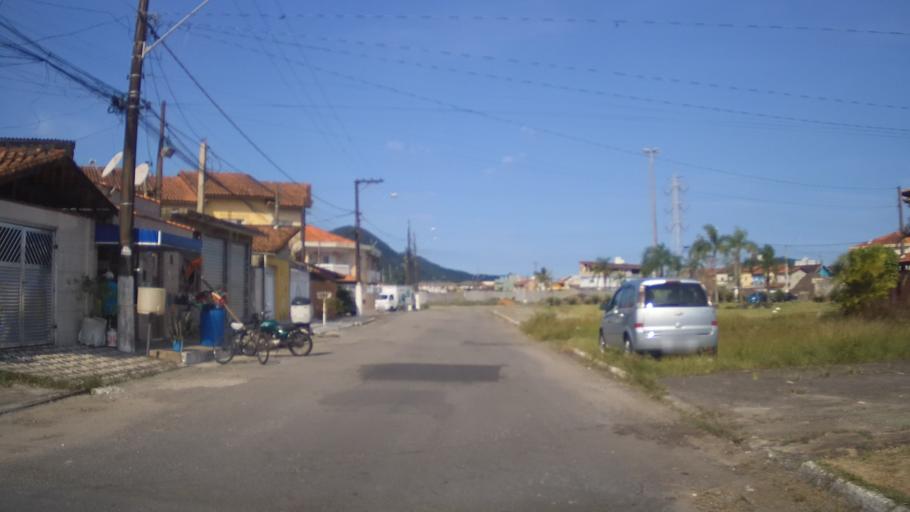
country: BR
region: Sao Paulo
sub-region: Praia Grande
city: Praia Grande
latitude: -23.9970
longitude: -46.4289
